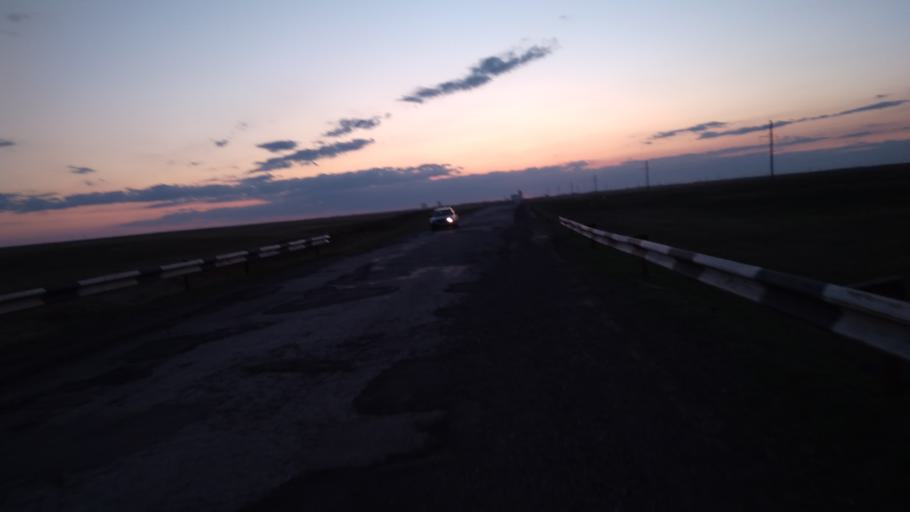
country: RU
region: Chelyabinsk
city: Troitsk
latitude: 54.0882
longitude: 61.6541
